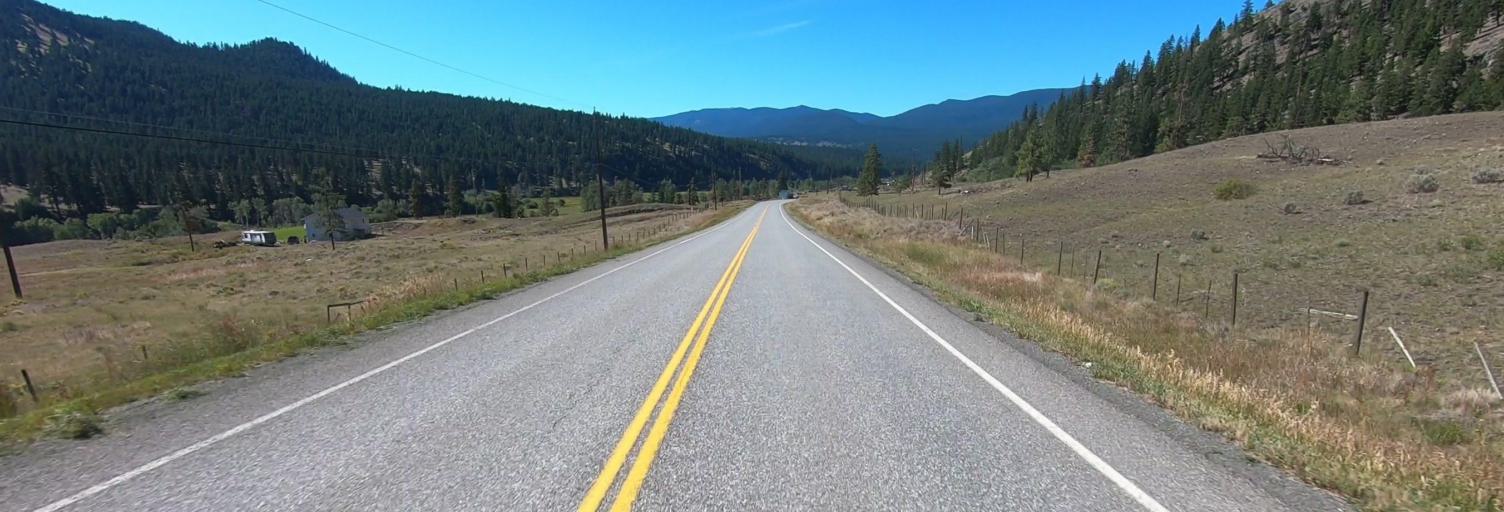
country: CA
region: British Columbia
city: Cache Creek
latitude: 50.8159
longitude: -121.5811
